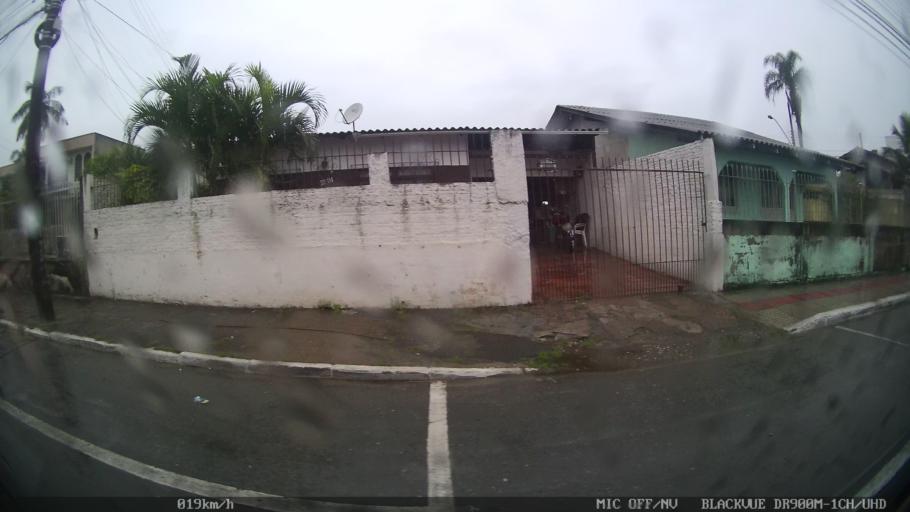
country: BR
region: Santa Catarina
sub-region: Itajai
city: Itajai
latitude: -26.9139
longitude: -48.6822
